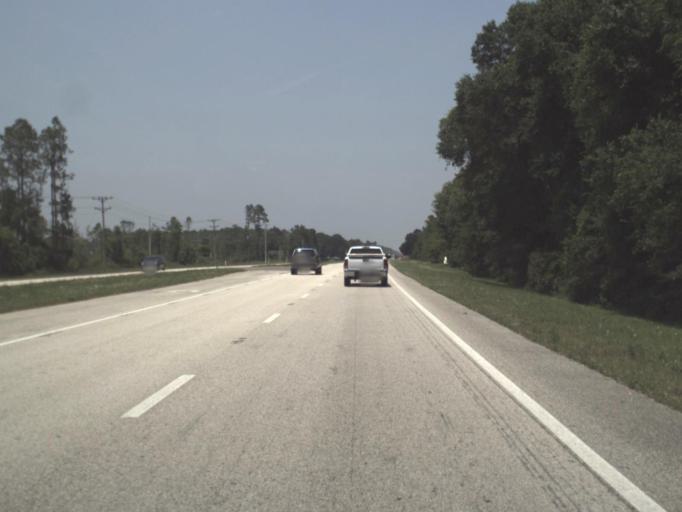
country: US
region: Florida
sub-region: Duval County
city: Baldwin
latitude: 30.1795
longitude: -82.0230
